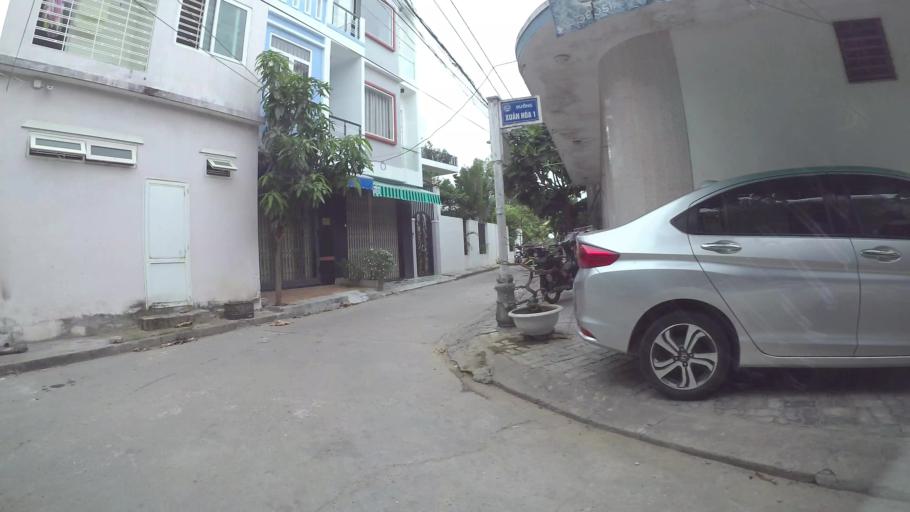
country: VN
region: Da Nang
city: Thanh Khe
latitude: 16.0676
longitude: 108.1906
